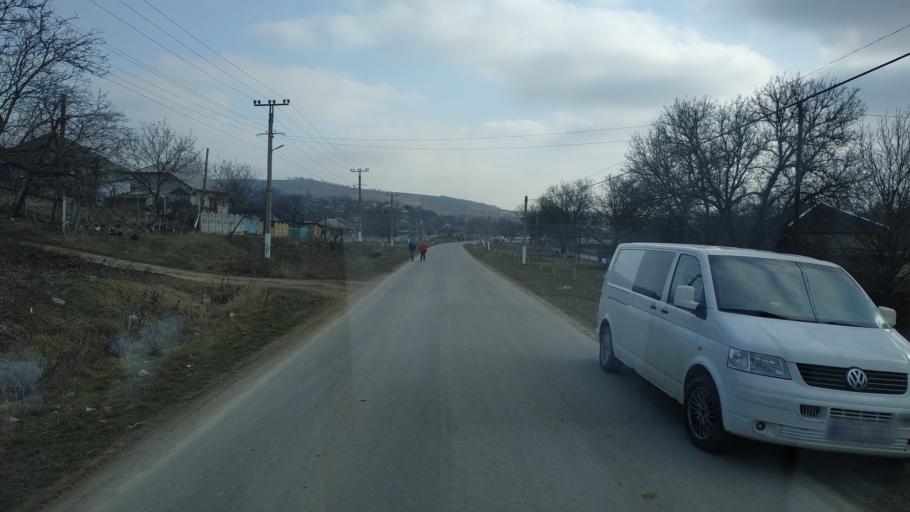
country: MD
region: Nisporeni
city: Nisporeni
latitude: 46.9406
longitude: 28.3260
